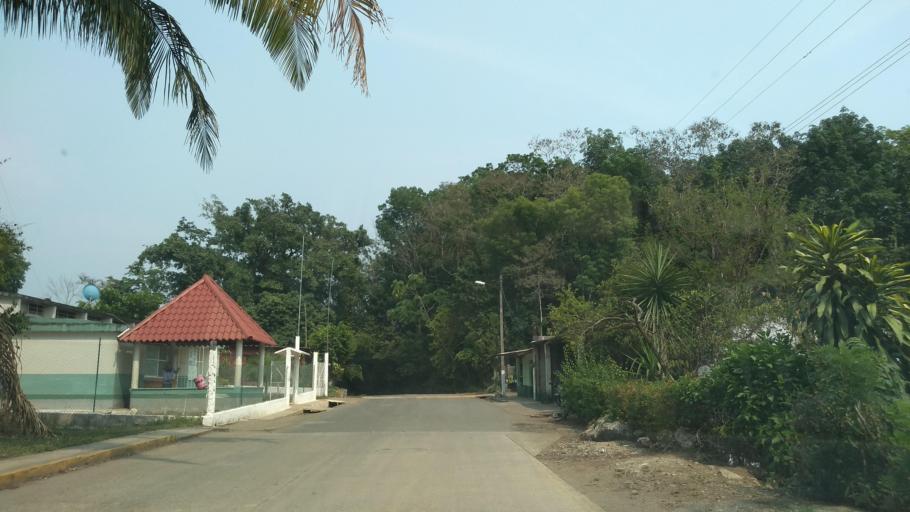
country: MX
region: Veracruz
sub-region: Tezonapa
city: Laguna Chica (Pueblo Nuevo)
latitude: 18.5424
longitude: -96.7751
